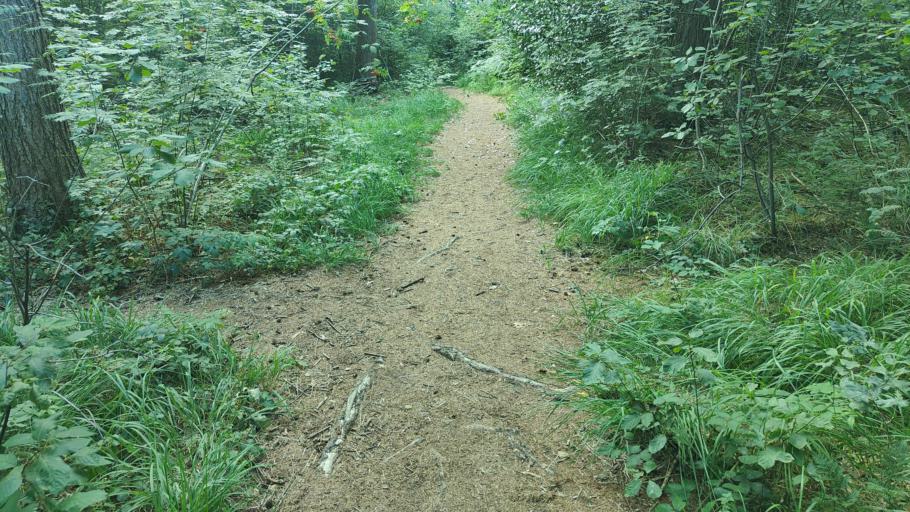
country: BE
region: Wallonia
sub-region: Province de Liege
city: La Calamine
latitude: 50.7041
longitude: 6.0440
